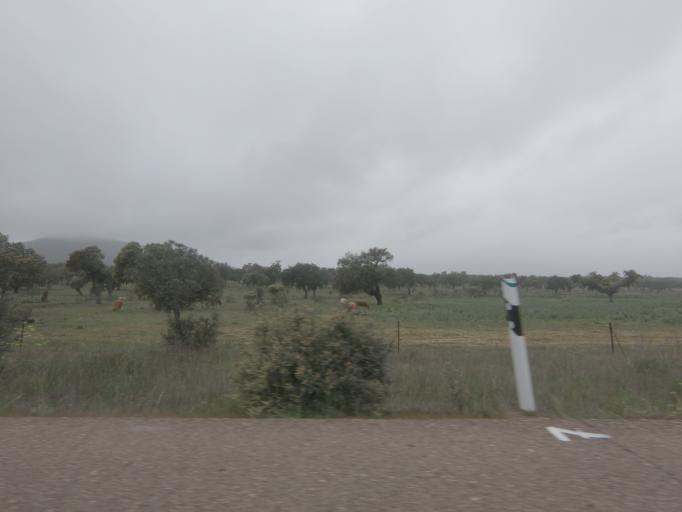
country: ES
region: Extremadura
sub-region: Provincia de Badajoz
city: Puebla de Obando
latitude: 39.1968
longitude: -6.5941
